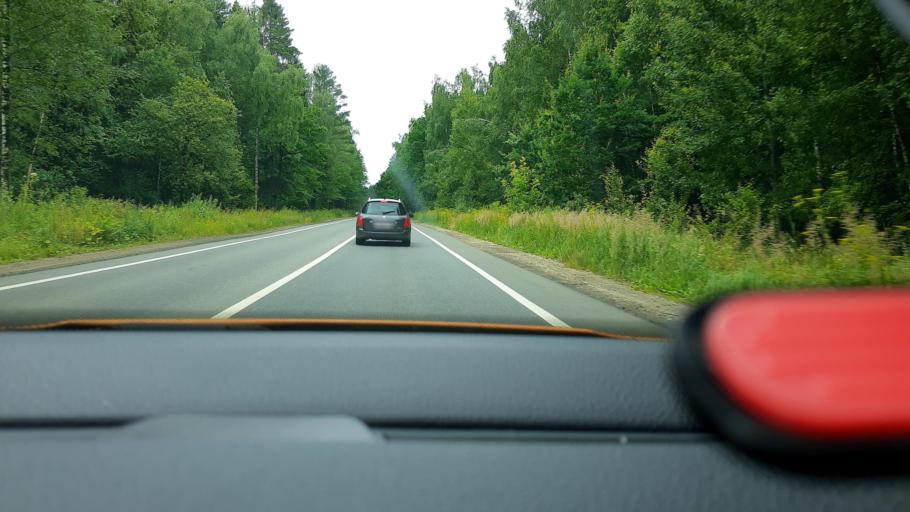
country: RU
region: Moskovskaya
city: Pirogovskiy
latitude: 55.9987
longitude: 37.6916
